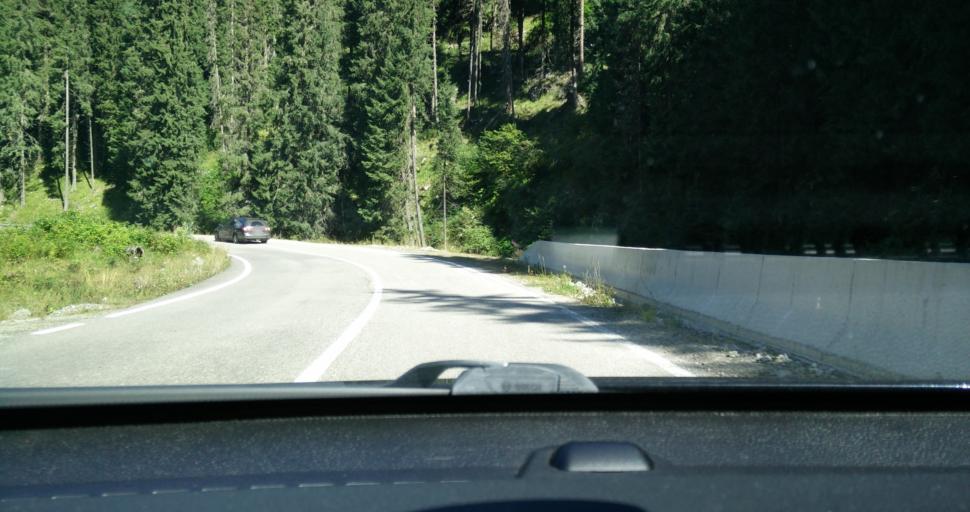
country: RO
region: Hunedoara
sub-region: Oras Petrila
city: Petrila
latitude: 45.5196
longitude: 23.6523
